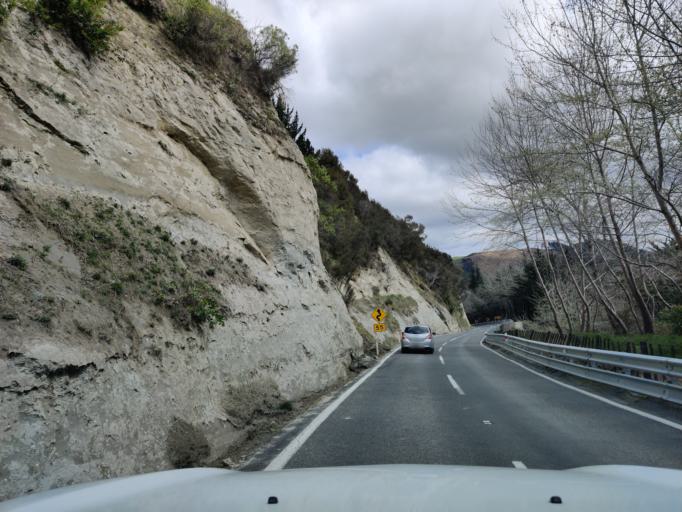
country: NZ
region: Manawatu-Wanganui
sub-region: Wanganui District
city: Wanganui
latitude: -39.7956
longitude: 175.2029
